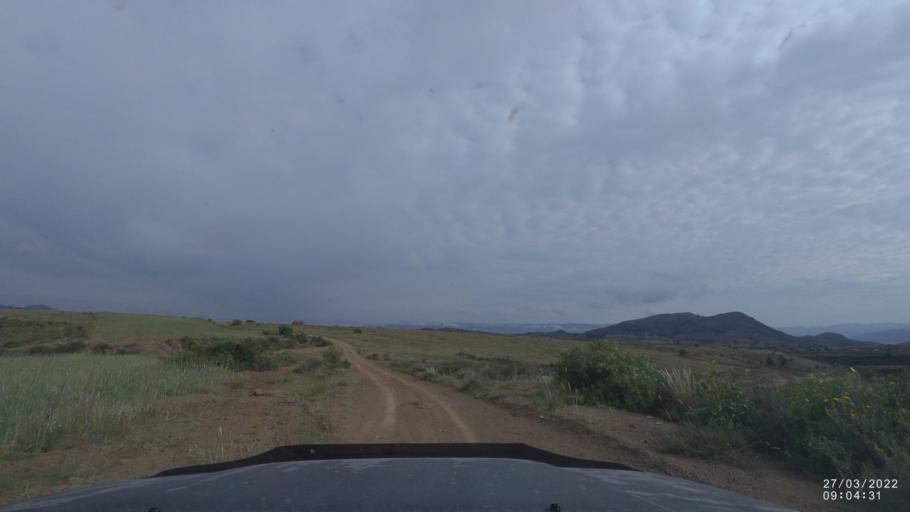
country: BO
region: Cochabamba
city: Cliza
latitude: -17.7341
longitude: -65.8650
